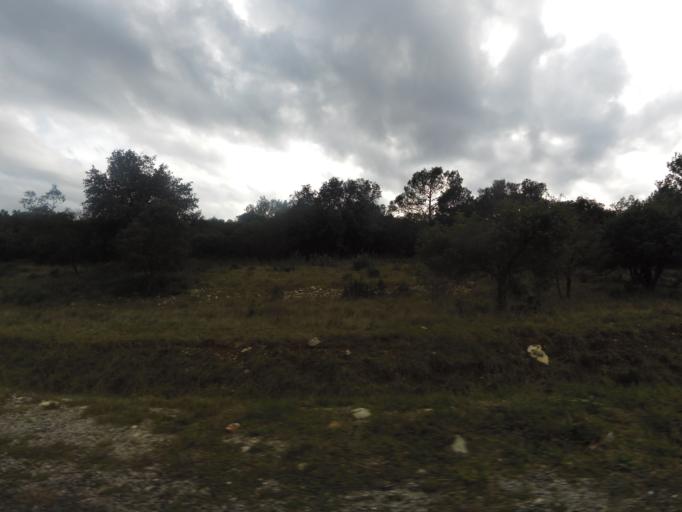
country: FR
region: Languedoc-Roussillon
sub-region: Departement du Gard
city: Saint-Mamert-du-Gard
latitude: 43.8619
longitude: 4.2057
